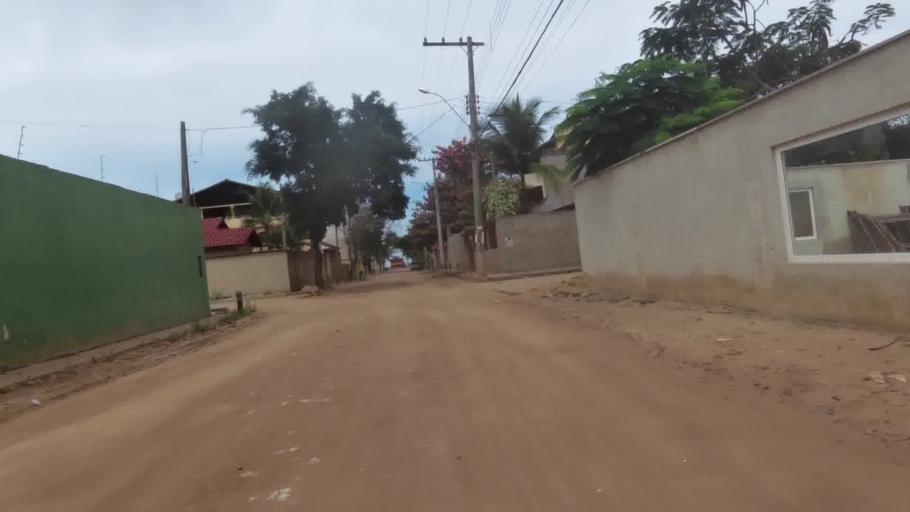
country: BR
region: Espirito Santo
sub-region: Piuma
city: Piuma
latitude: -20.8424
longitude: -40.7363
